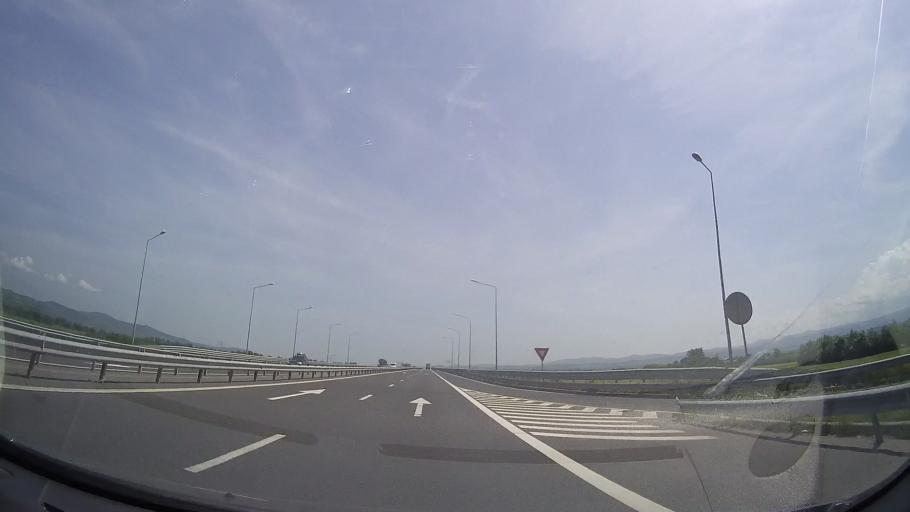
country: RO
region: Hunedoara
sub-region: Comuna Turdas
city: Pricaz
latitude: 45.8774
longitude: 23.1918
